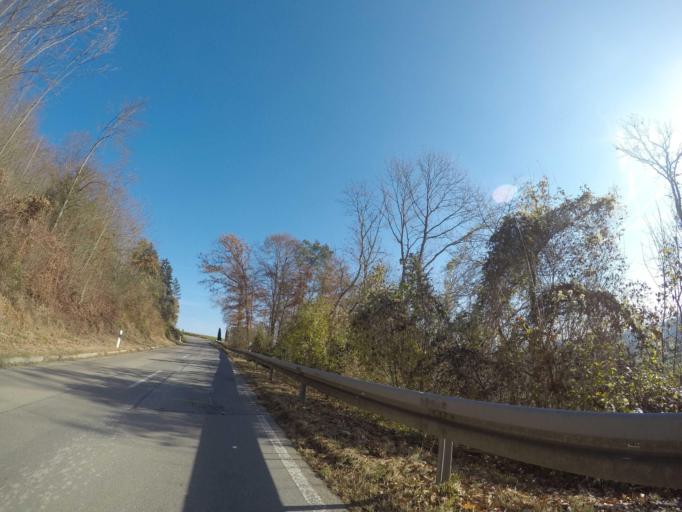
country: DE
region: Baden-Wuerttemberg
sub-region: Tuebingen Region
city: Emeringen
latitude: 48.2211
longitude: 9.5185
